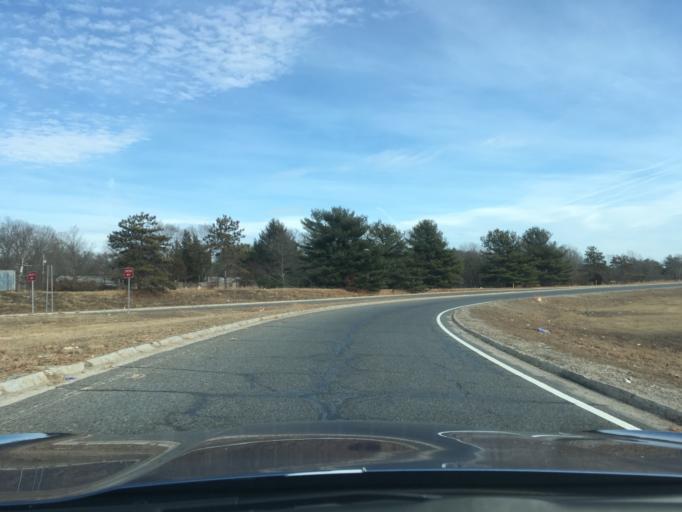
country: US
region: Massachusetts
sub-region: Bristol County
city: North Seekonk
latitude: 41.9044
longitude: -71.3557
